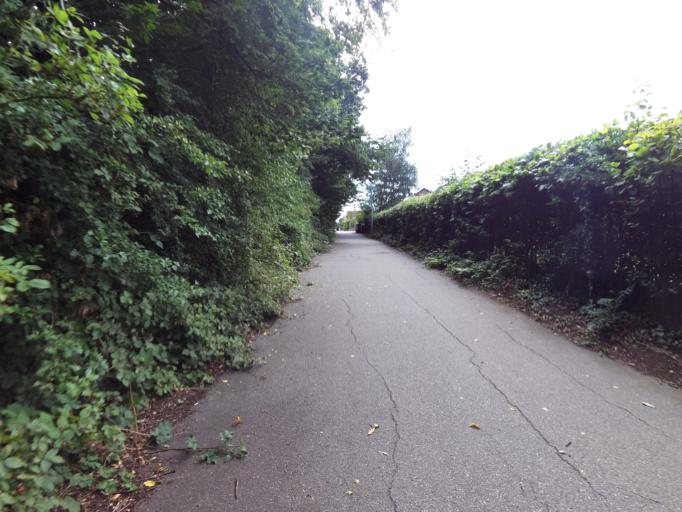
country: GB
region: England
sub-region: Essex
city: Colchester
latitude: 51.9086
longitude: 0.9174
